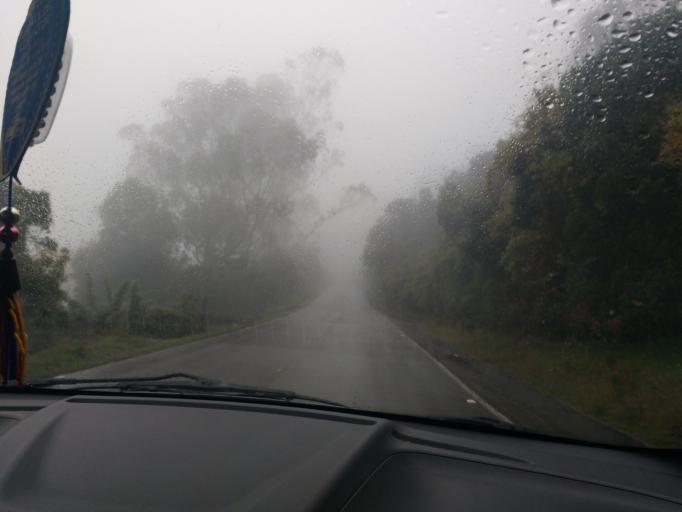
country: CO
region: Bogota D.C.
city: Bogota
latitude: 4.5920
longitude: -74.0279
